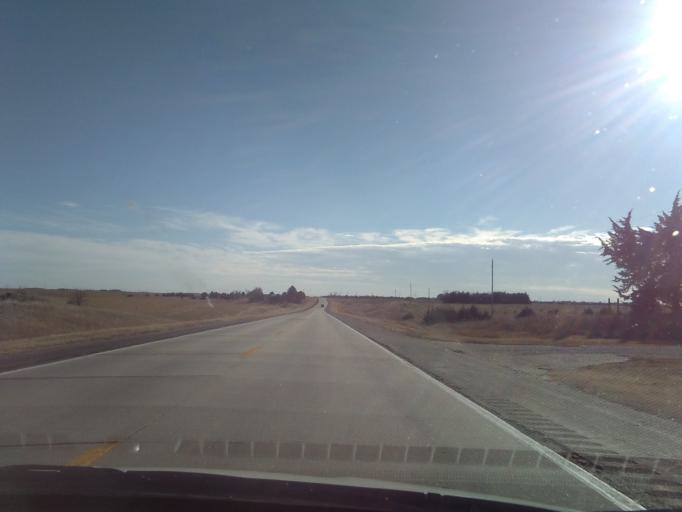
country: US
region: Nebraska
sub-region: Adams County
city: Hastings
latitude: 40.4007
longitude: -98.4399
